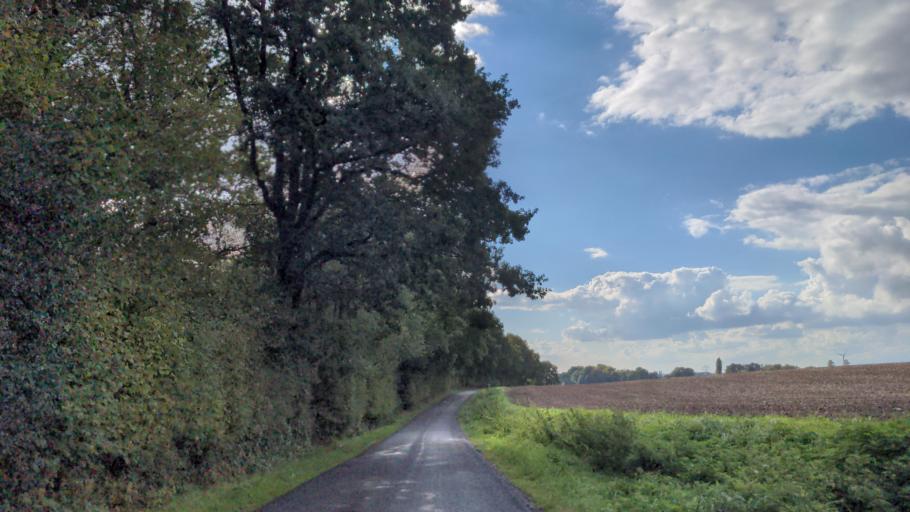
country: DE
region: Schleswig-Holstein
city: Stockelsdorf
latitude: 53.9270
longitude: 10.6250
